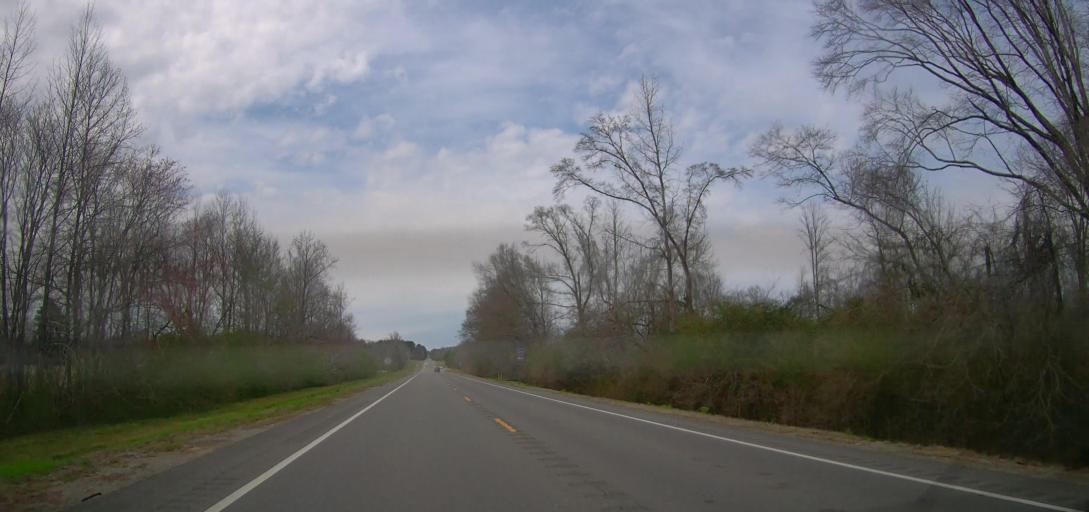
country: US
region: Alabama
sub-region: Marion County
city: Guin
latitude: 33.9992
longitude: -87.9310
